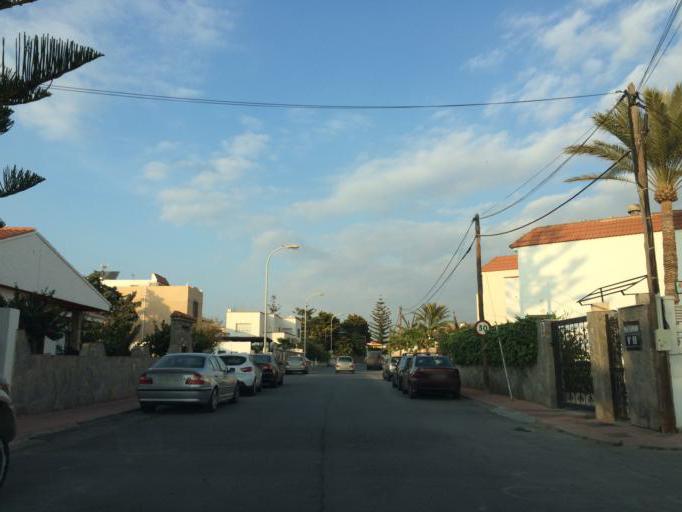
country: ES
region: Andalusia
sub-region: Provincia de Almeria
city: Almeria
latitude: 36.8219
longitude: -2.4366
